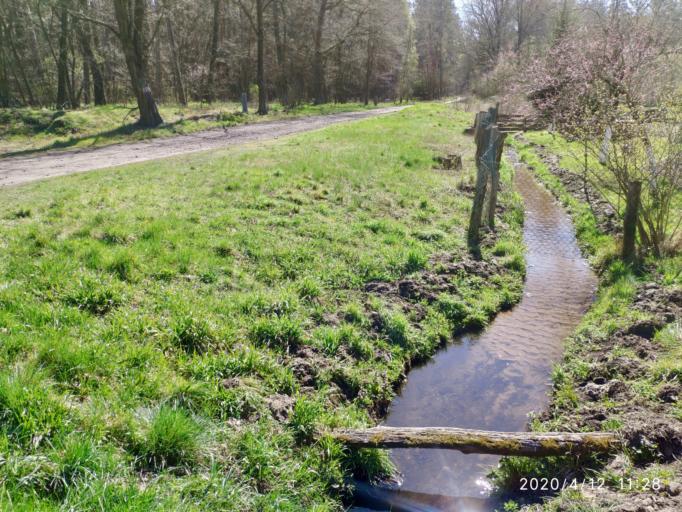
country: PL
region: Lubusz
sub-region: Powiat krosnienski
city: Dabie
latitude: 52.0393
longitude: 15.2331
